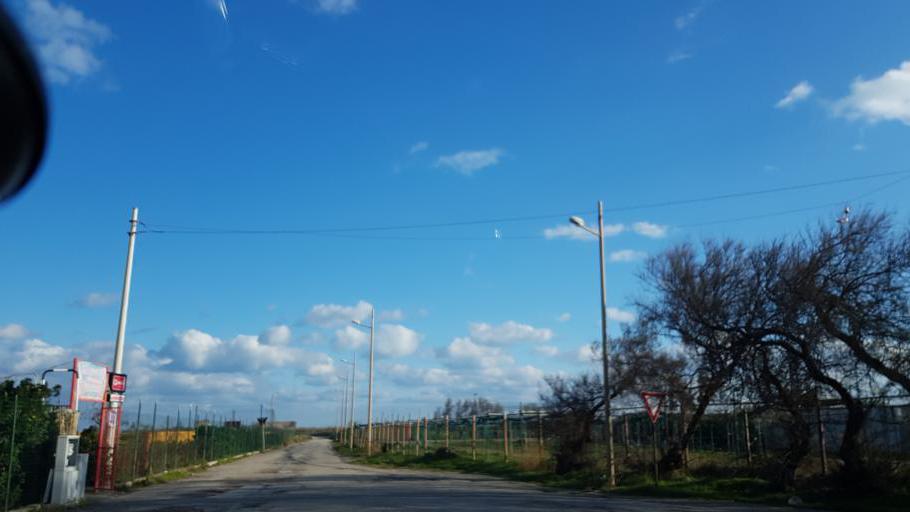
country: IT
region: Apulia
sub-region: Provincia di Brindisi
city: Materdomini
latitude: 40.6799
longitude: 17.9333
